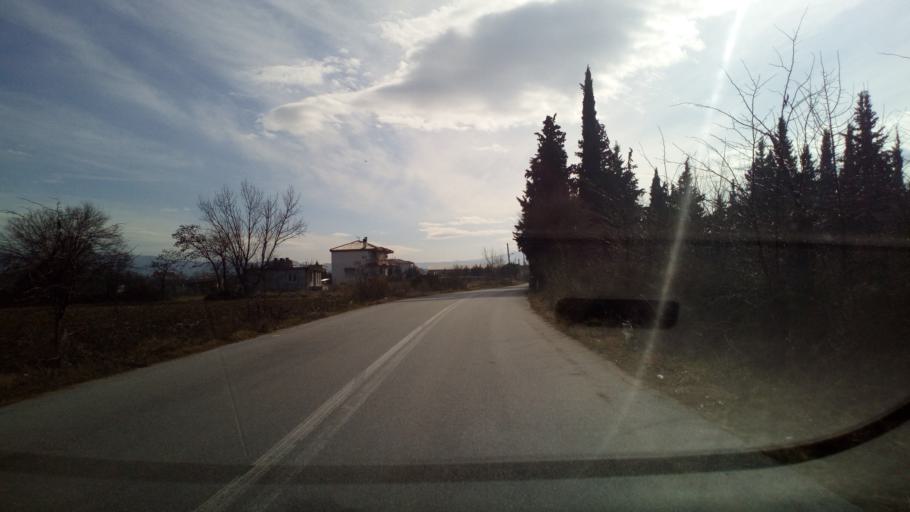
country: GR
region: Central Macedonia
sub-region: Nomos Thessalonikis
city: Gerakarou
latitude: 40.6417
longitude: 23.2464
